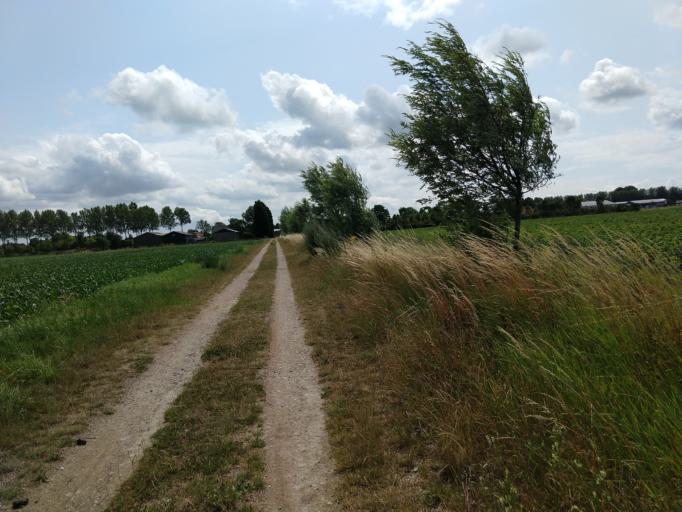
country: NL
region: Zeeland
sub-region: Gemeente Goes
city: Goes
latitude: 51.4810
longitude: 3.8109
